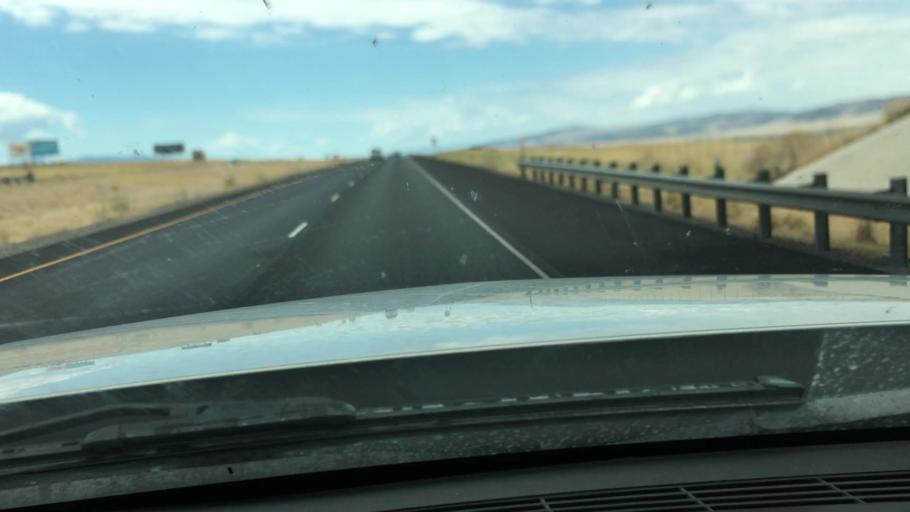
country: US
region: Utah
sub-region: Juab County
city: Mona
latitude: 39.8071
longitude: -111.8358
